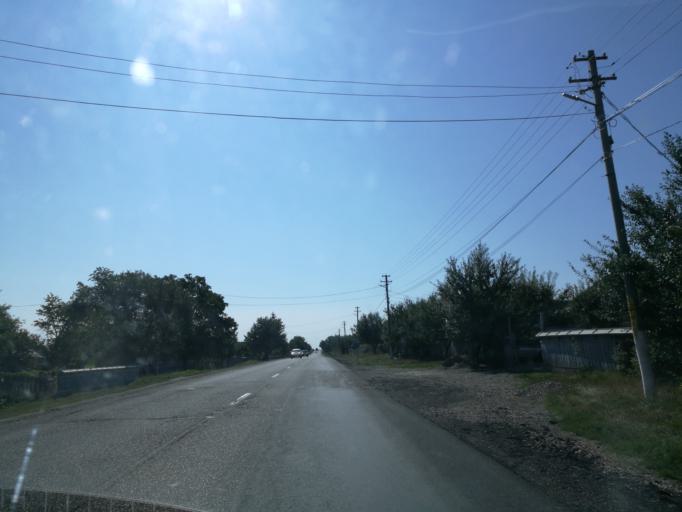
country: RO
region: Suceava
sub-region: Comuna Draguseni
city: Draguseni
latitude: 47.2838
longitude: 26.5034
